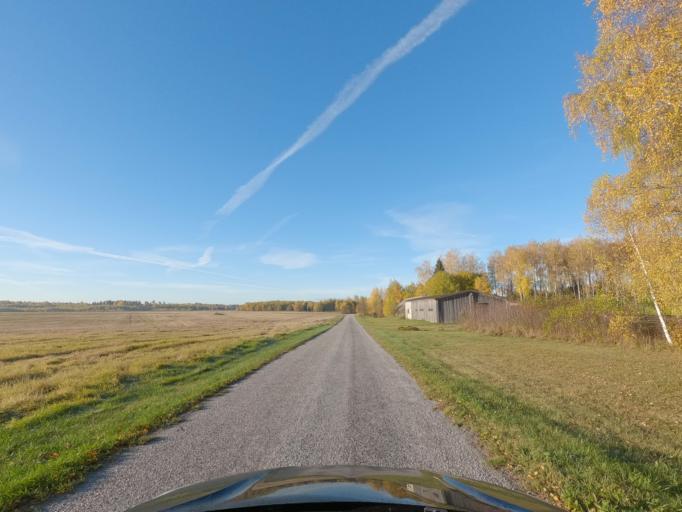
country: EE
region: Raplamaa
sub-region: Rapla vald
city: Rapla
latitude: 59.0614
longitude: 24.8443
